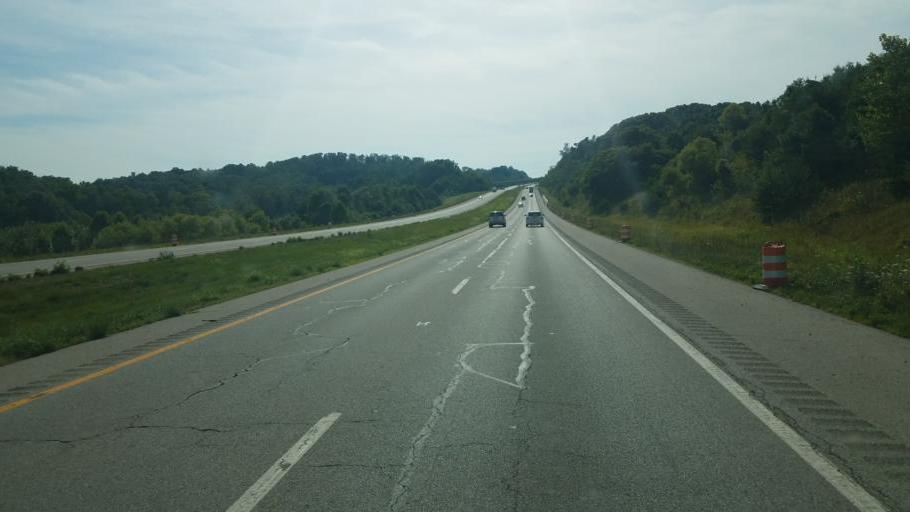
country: US
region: Ohio
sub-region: Fairfield County
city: Lancaster
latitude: 39.6677
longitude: -82.5873
